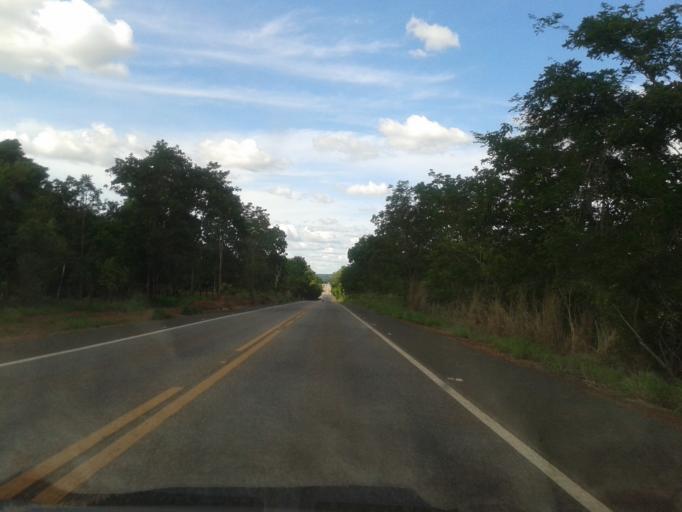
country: BR
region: Goias
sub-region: Mozarlandia
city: Mozarlandia
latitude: -15.0202
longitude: -50.5969
